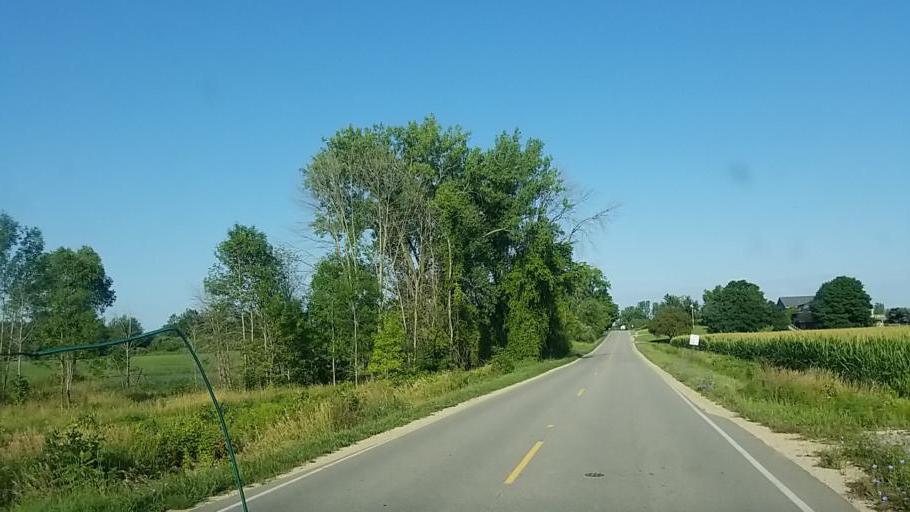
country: US
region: Michigan
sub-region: Newaygo County
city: Newaygo
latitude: 43.3511
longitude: -85.8305
